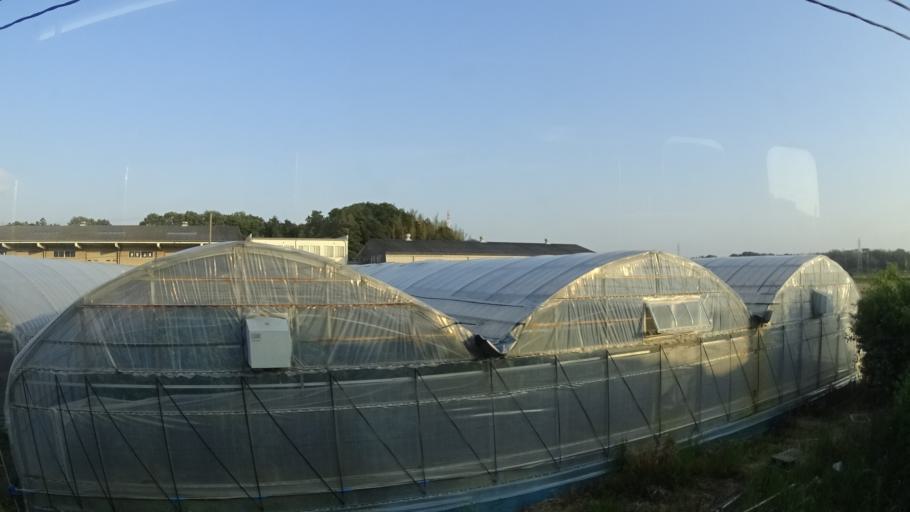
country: JP
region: Aichi
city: Tahara
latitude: 34.6919
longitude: 137.3333
